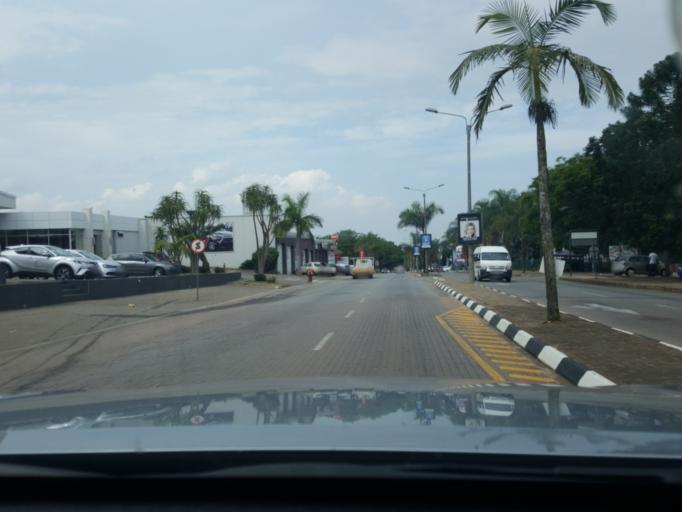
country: ZA
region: Mpumalanga
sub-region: Ehlanzeni District
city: White River
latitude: -25.3313
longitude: 31.0119
